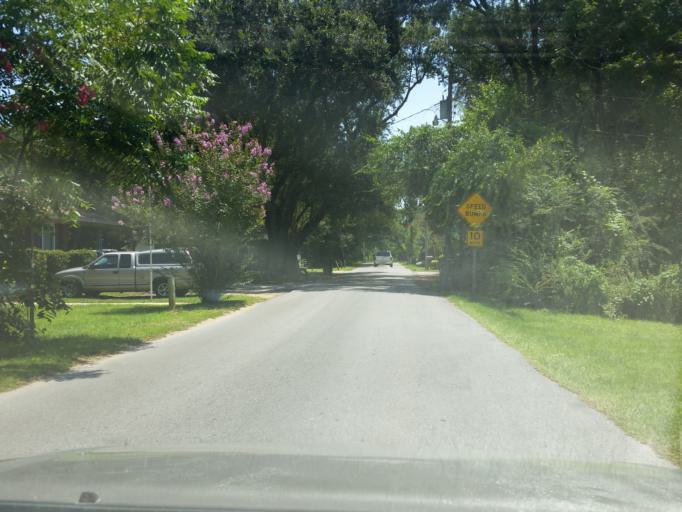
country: US
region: Florida
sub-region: Escambia County
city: Ferry Pass
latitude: 30.5086
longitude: -87.2270
